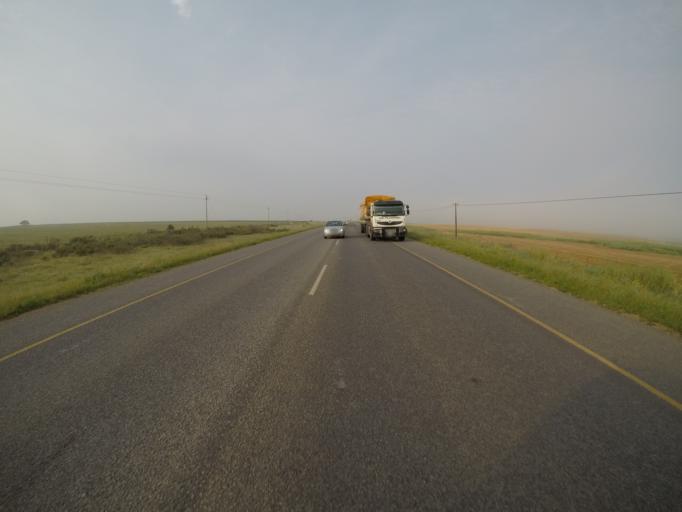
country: ZA
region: Western Cape
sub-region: West Coast District Municipality
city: Malmesbury
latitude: -33.6518
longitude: 18.7100
